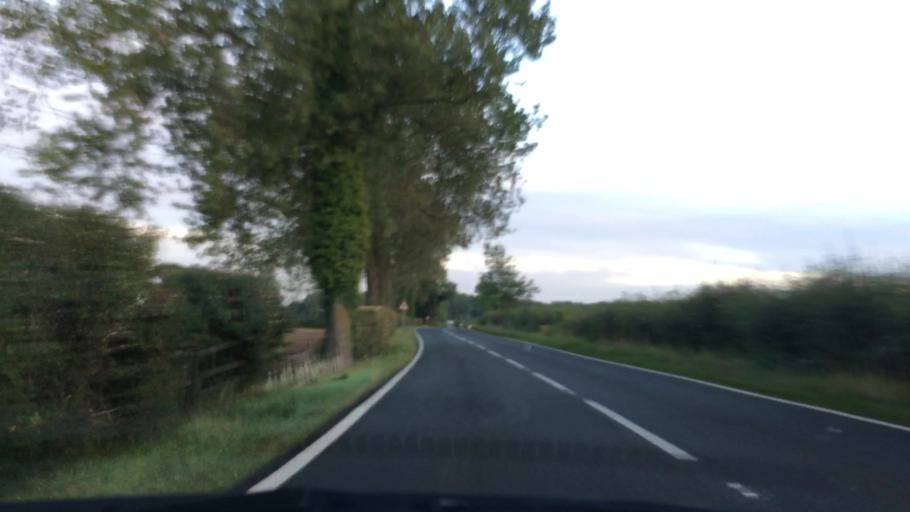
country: GB
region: England
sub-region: North East Lincolnshire
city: Wold Newton
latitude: 53.4588
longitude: -0.0913
